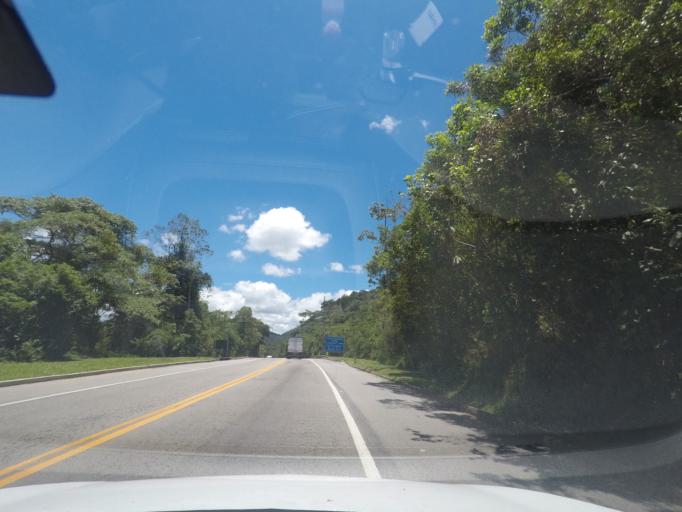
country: BR
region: Rio de Janeiro
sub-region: Teresopolis
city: Teresopolis
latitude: -22.4612
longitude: -42.9820
